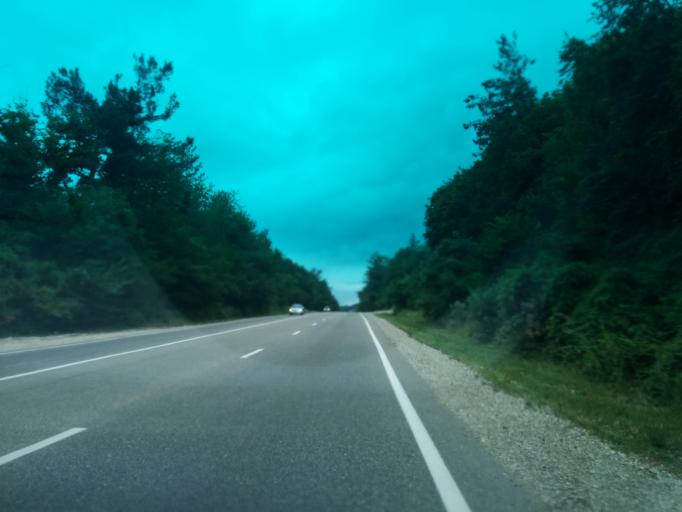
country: RU
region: Krasnodarskiy
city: Ol'ginka
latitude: 44.1792
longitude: 38.9390
